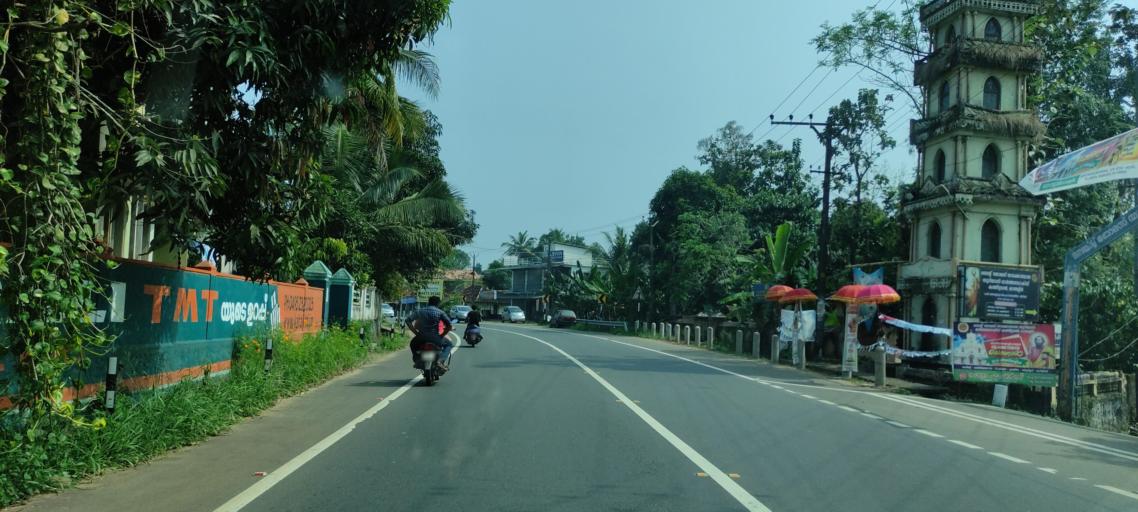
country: IN
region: Kerala
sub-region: Alappuzha
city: Chengannur
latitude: 9.2502
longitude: 76.6653
